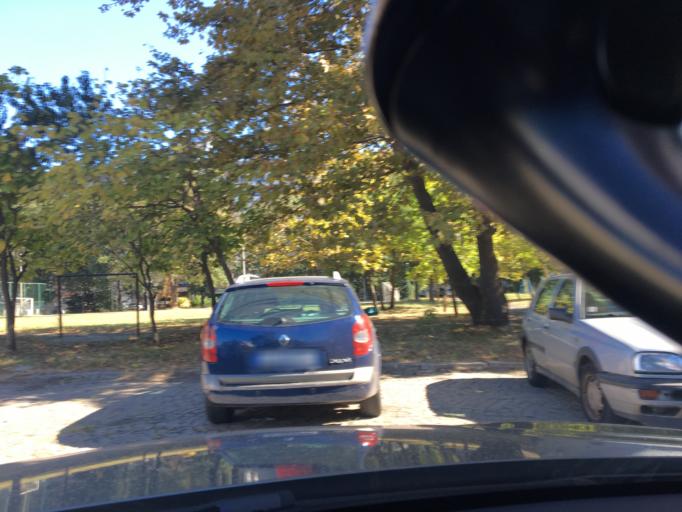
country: BG
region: Burgas
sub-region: Obshtina Burgas
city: Burgas
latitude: 42.5160
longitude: 27.4584
